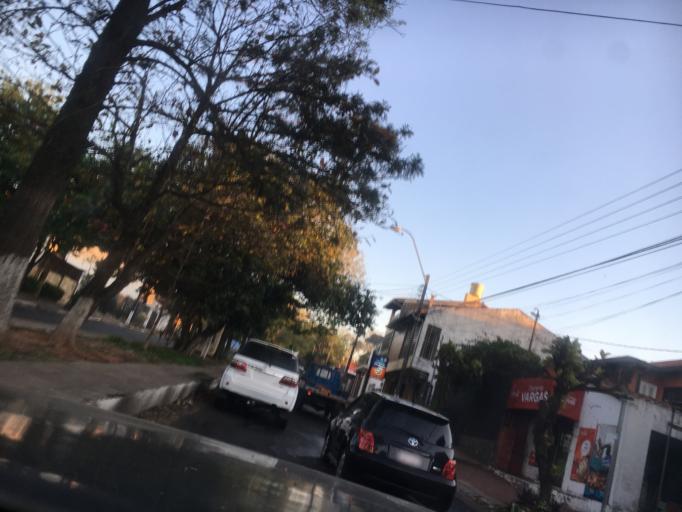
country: PY
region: Central
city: Lambare
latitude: -25.3336
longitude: -57.6078
